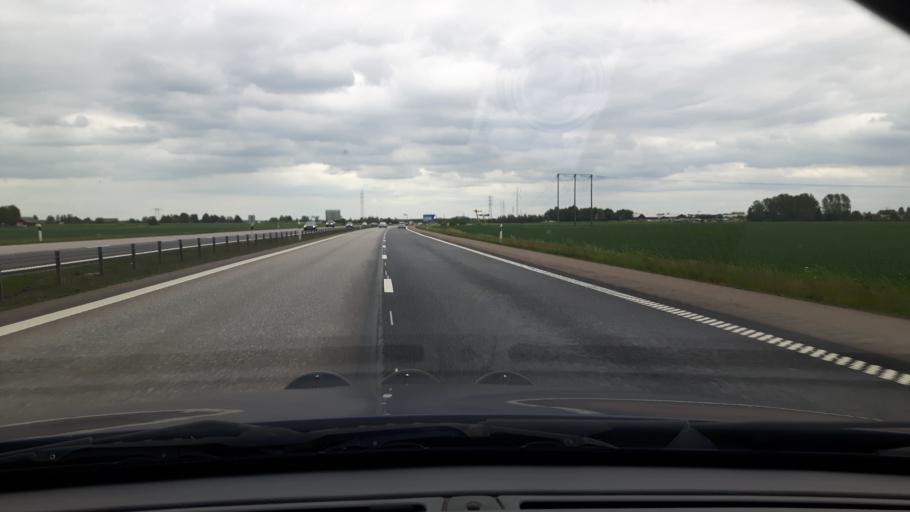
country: SE
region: OEstergoetland
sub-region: Linkopings Kommun
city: Malmslatt
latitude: 58.4388
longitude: 15.5635
